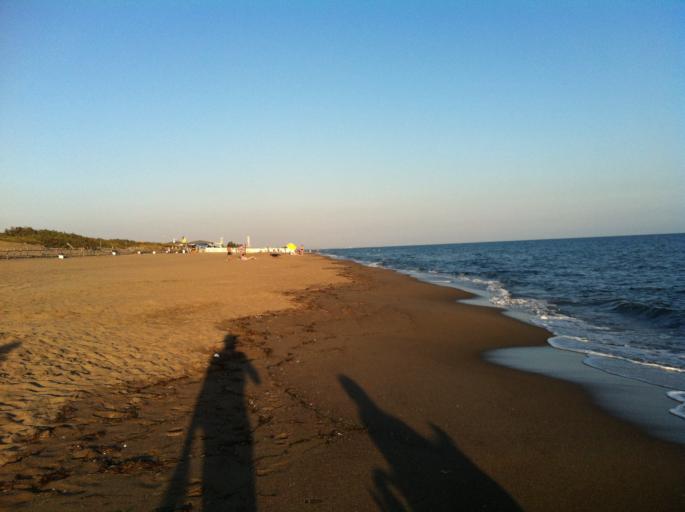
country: IT
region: Latium
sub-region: Provincia di Viterbo
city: Pescia Romana
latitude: 42.3800
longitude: 11.4419
